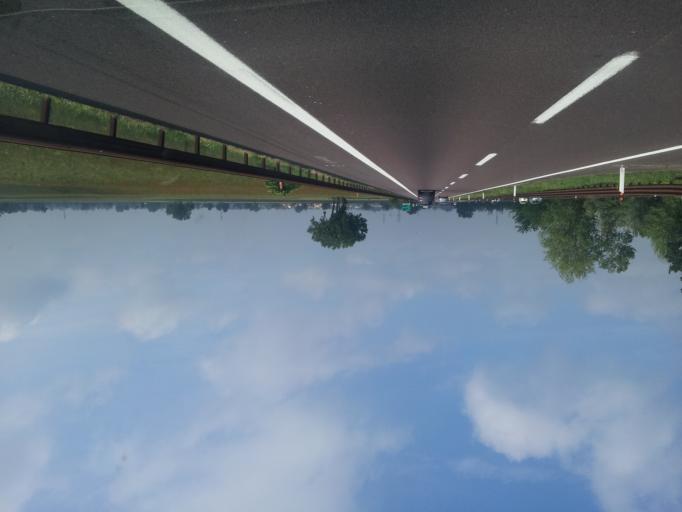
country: IT
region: Lombardy
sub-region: Provincia di Mantova
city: Pegognaga
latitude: 44.9716
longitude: 10.8573
